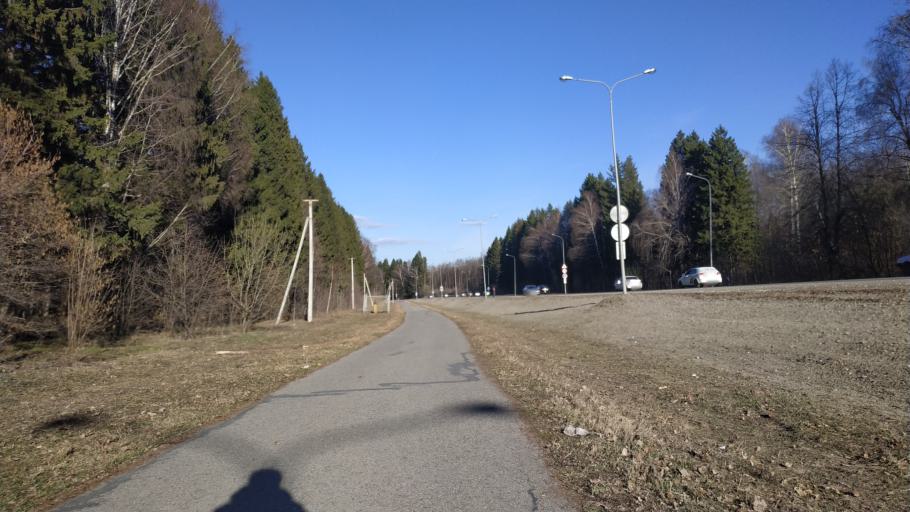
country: RU
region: Chuvashia
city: Novyye Lapsary
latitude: 56.1279
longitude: 47.1218
